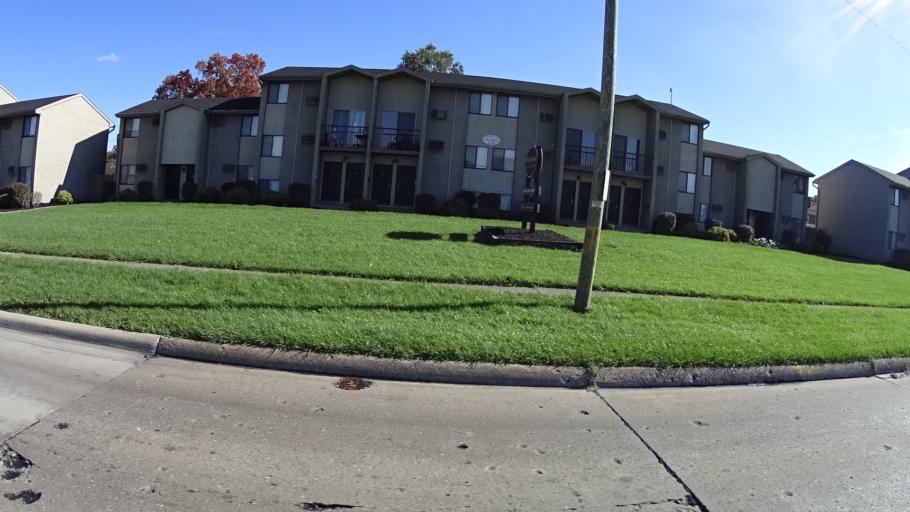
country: US
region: Ohio
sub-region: Lorain County
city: Lorain
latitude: 41.4480
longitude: -82.1792
